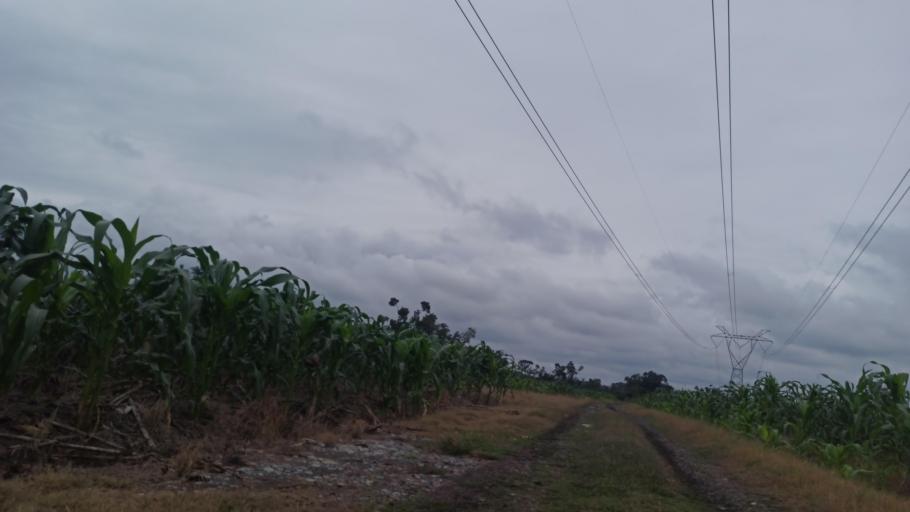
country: MX
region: Puebla
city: Espinal
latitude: 20.3039
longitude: -97.4113
